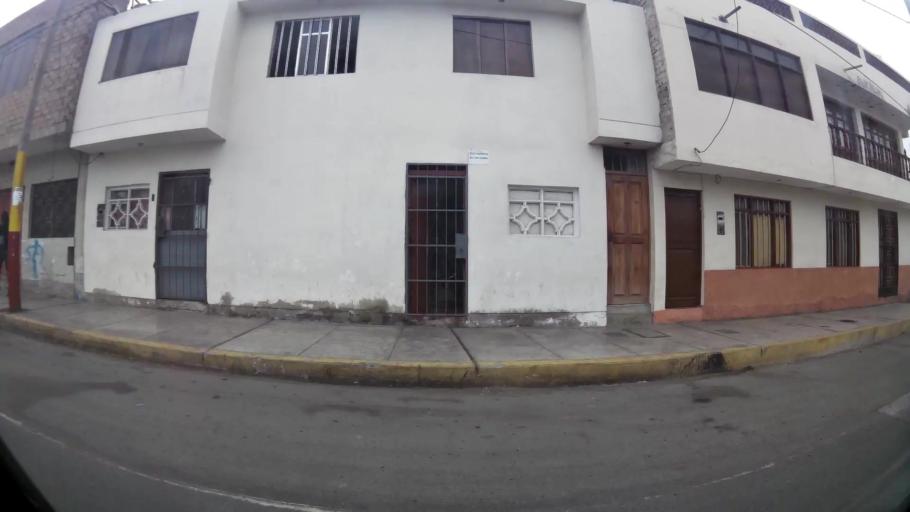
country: PE
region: Ancash
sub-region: Provincia de Santa
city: Chimbote
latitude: -9.0738
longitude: -78.5862
